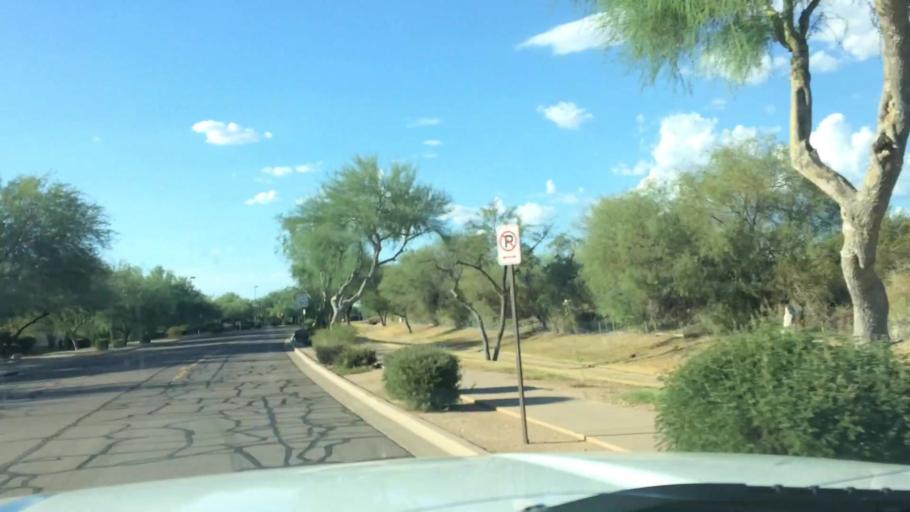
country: US
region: Arizona
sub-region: Maricopa County
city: Paradise Valley
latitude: 33.6464
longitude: -111.9028
